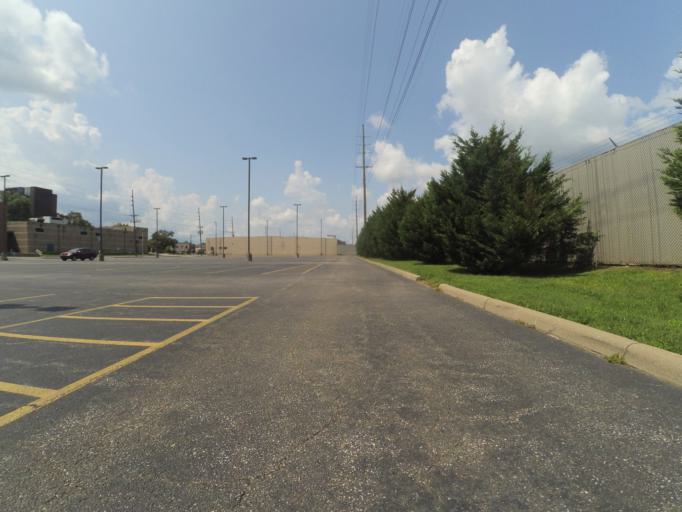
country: US
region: West Virginia
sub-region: Cabell County
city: Huntington
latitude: 38.4256
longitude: -82.4302
